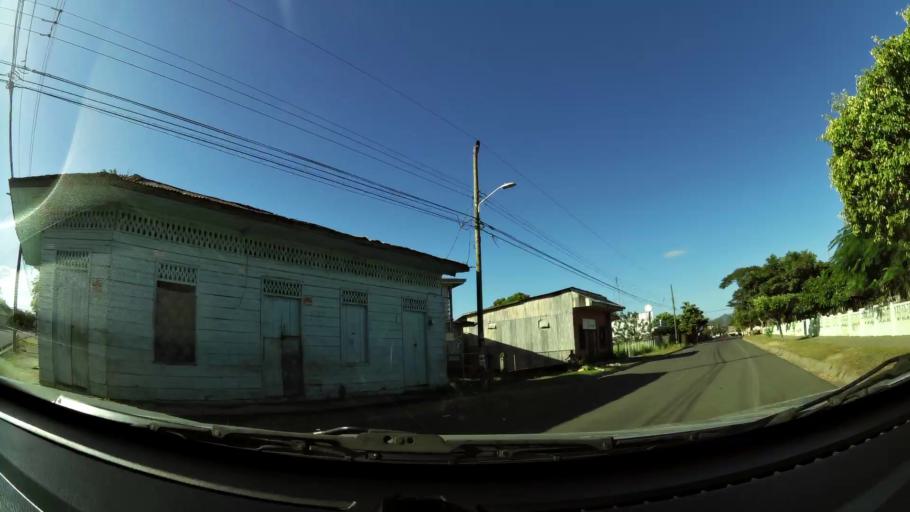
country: CR
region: Guanacaste
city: Belen
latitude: 10.4450
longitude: -85.5494
